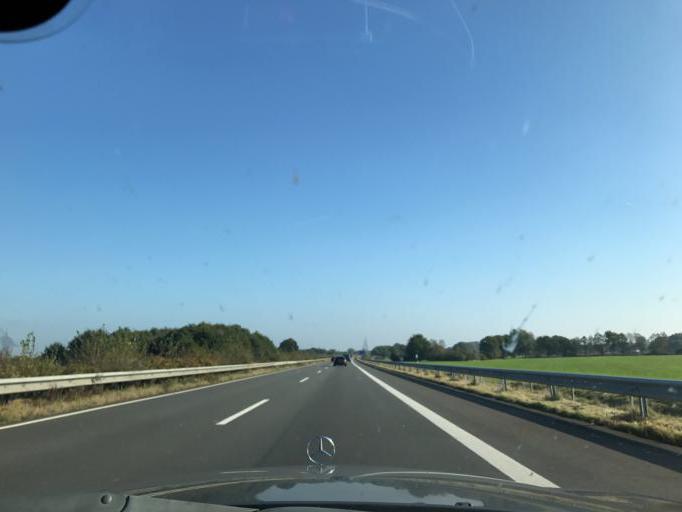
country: DE
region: Lower Saxony
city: Westerstede
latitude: 53.2854
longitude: 7.8813
